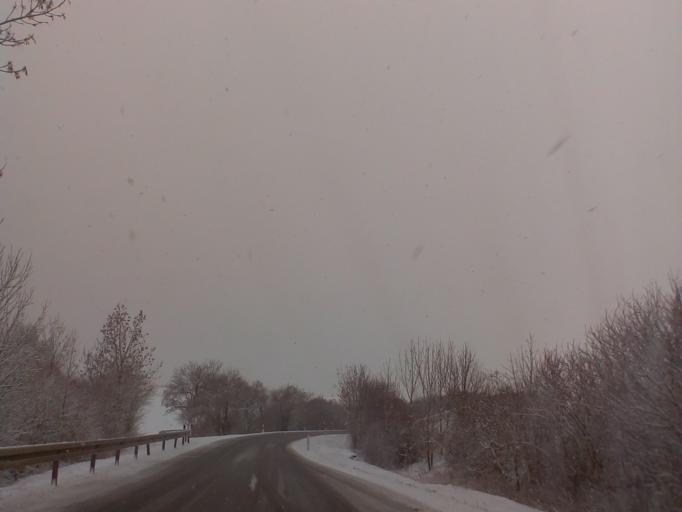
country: DE
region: Thuringia
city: Apfelstadt
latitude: 50.8509
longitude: 10.8728
